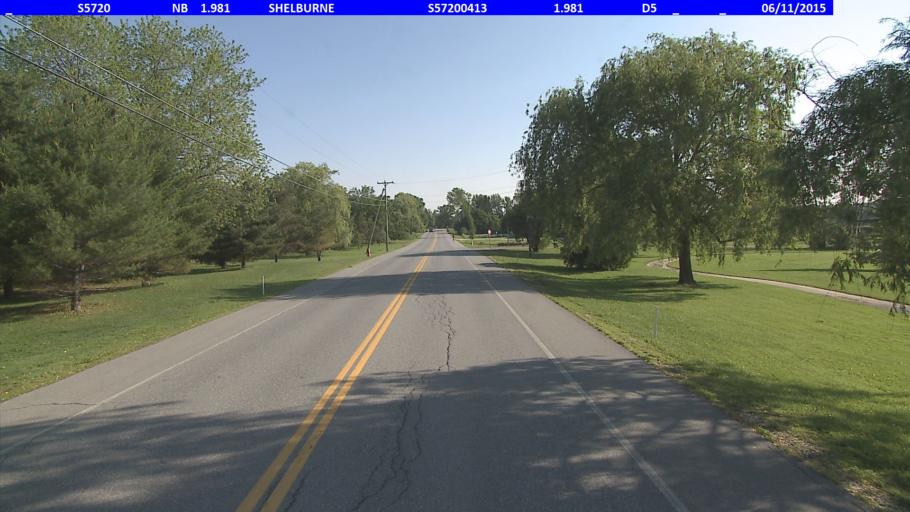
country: US
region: Vermont
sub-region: Chittenden County
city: South Burlington
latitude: 44.3962
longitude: -73.2006
